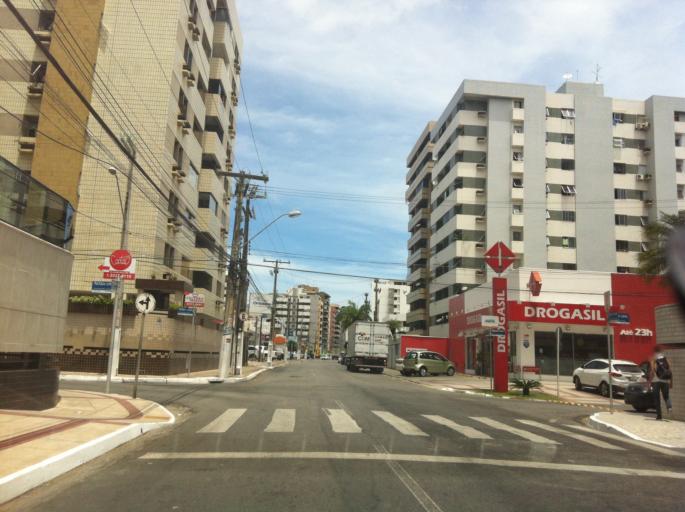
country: BR
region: Alagoas
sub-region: Maceio
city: Maceio
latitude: -9.6620
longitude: -35.7033
